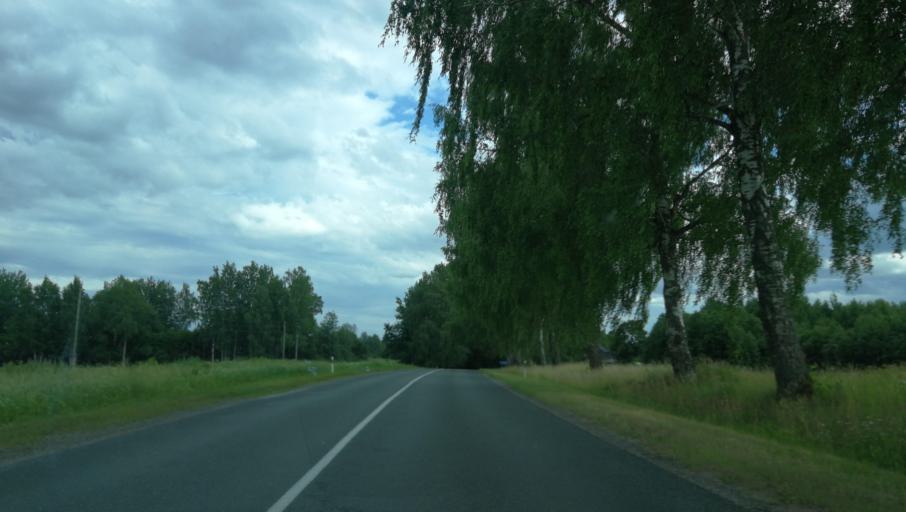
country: LV
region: Rujienas
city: Rujiena
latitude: 57.8644
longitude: 25.3715
